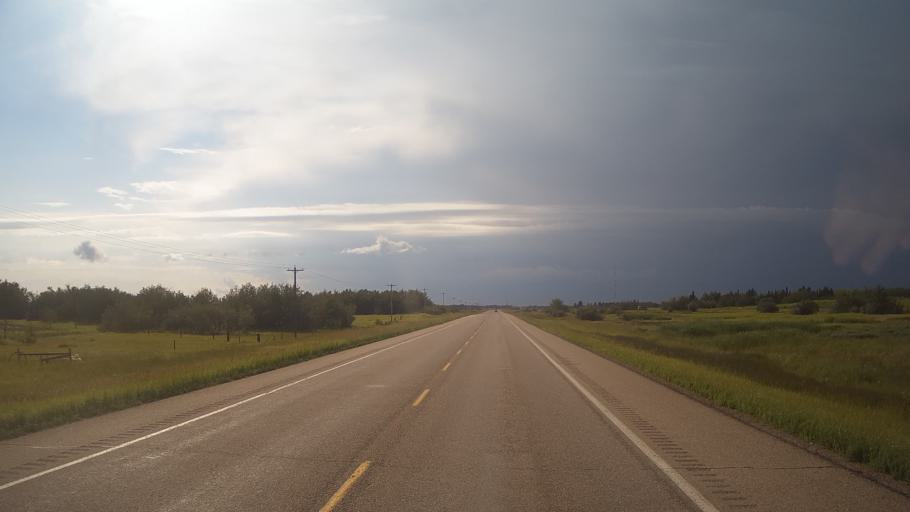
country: CA
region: Alberta
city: Viking
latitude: 53.1679
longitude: -112.0309
